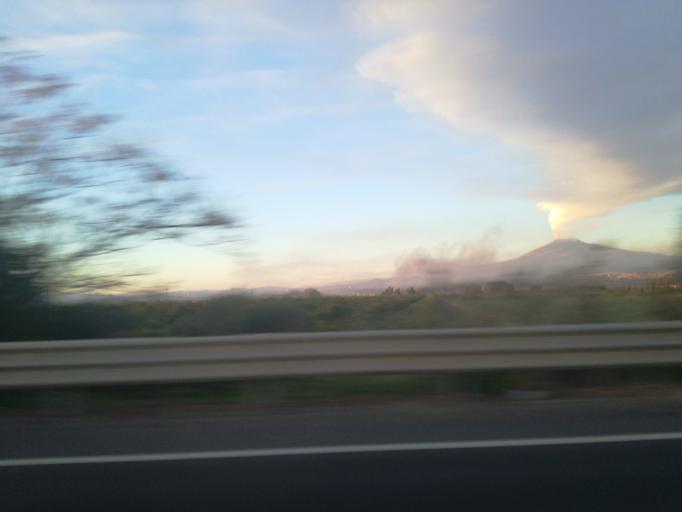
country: IT
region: Sicily
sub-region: Catania
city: Motta Sant'Anastasia
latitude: 37.4300
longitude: 14.9398
